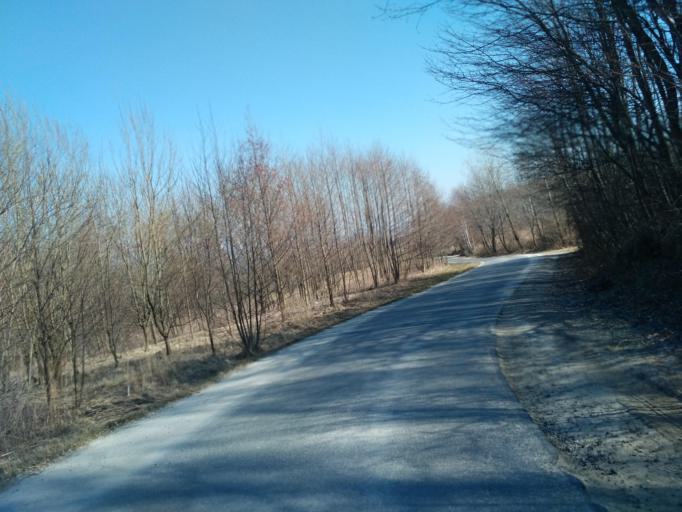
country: PL
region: Subcarpathian Voivodeship
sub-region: Powiat strzyzowski
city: Czudec
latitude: 49.9725
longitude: 21.8490
